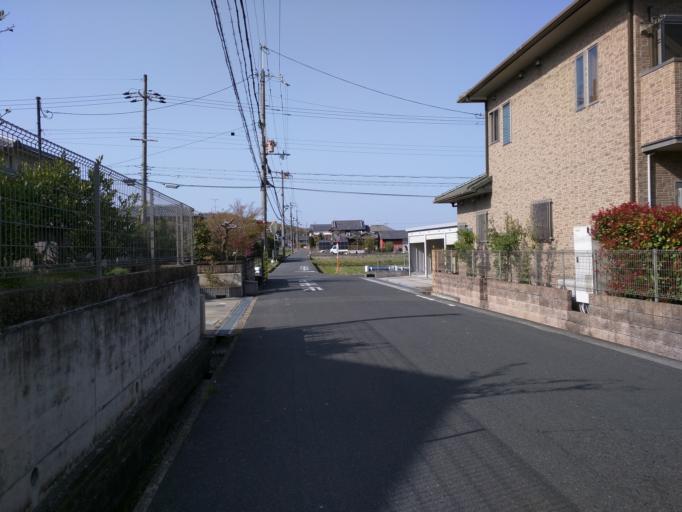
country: JP
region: Kyoto
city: Tanabe
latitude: 34.7628
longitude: 135.7841
